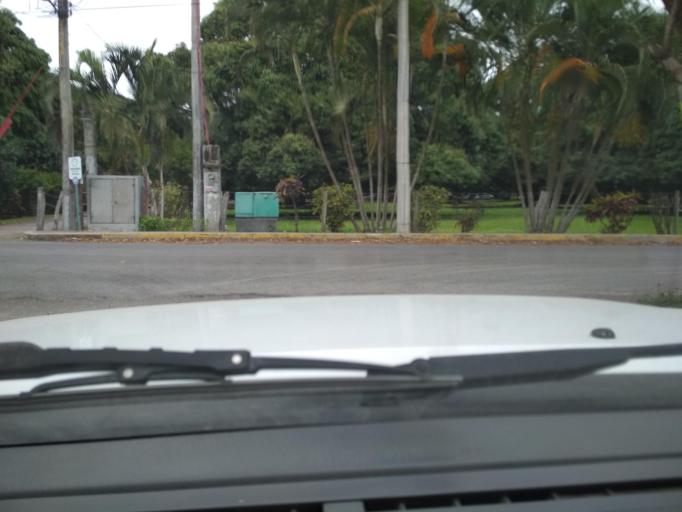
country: MX
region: Veracruz
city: Paso del Toro
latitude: 19.0555
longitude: -96.1360
